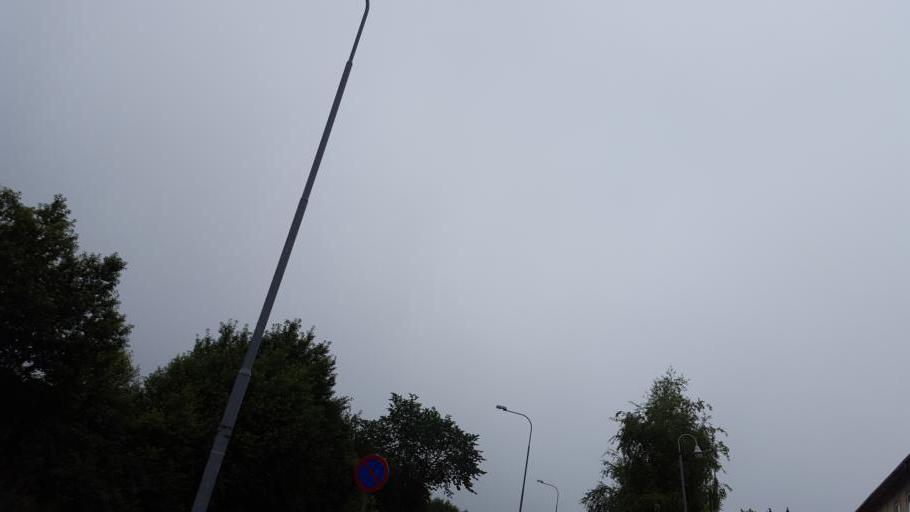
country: SE
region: Stockholm
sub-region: Upplands Vasby Kommun
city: Upplands Vaesby
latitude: 59.5071
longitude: 17.8843
